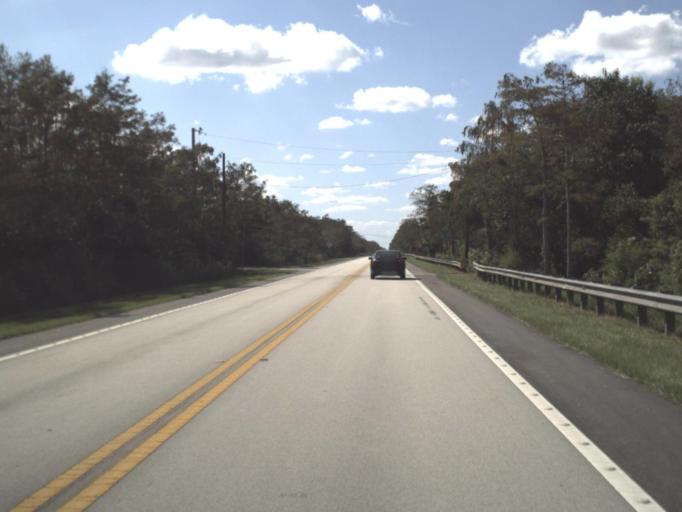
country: US
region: Florida
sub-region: Miami-Dade County
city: Kendall West
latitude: 25.8463
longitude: -80.9282
